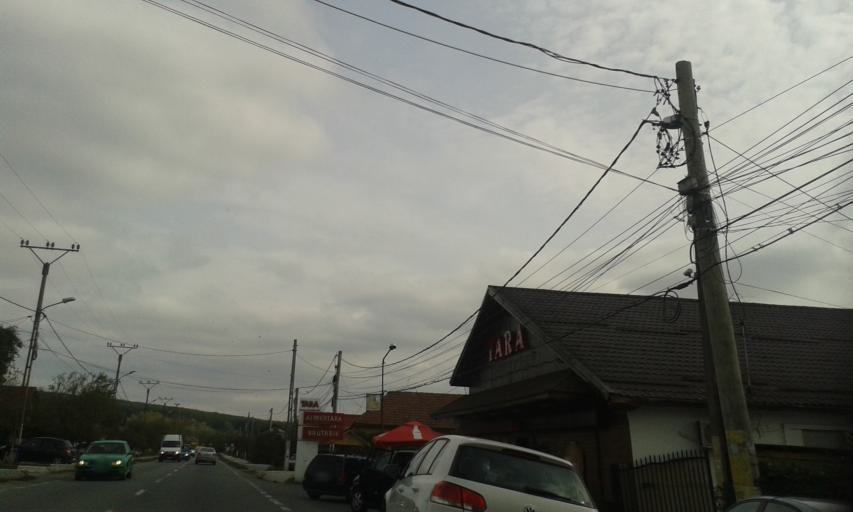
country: RO
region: Gorj
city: Targu Jiu
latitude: 45.0422
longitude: 23.3397
